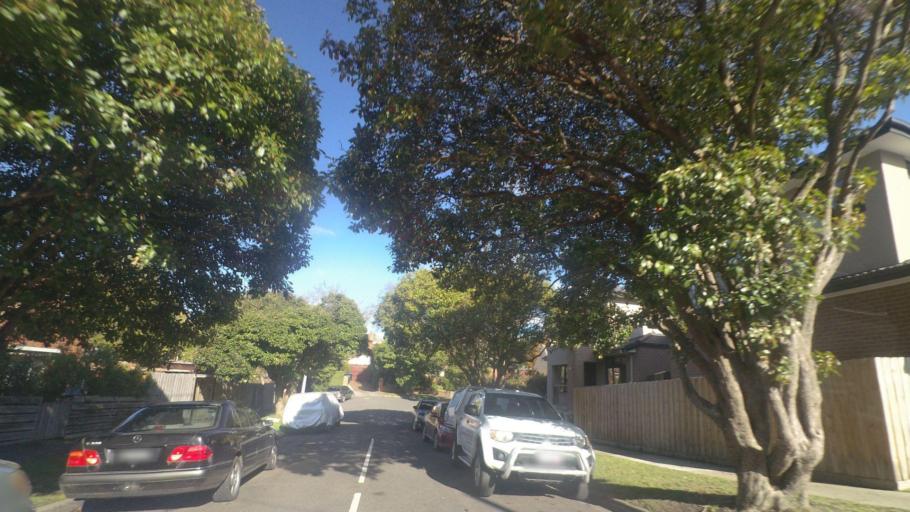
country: AU
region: Victoria
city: Mont Albert
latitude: -37.8116
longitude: 145.1085
